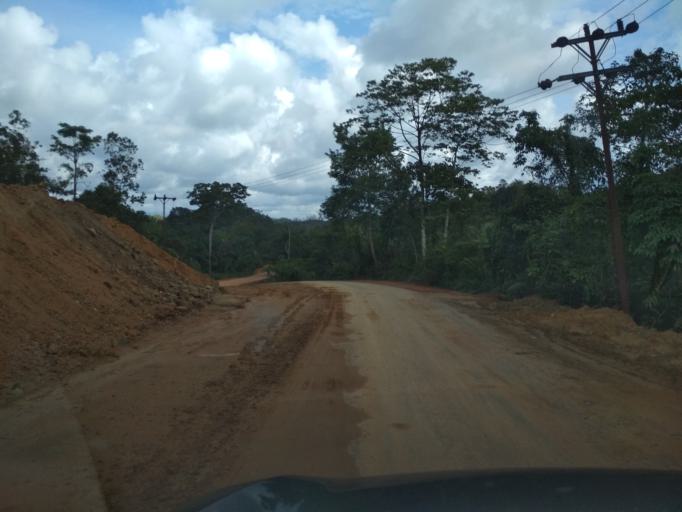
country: ID
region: West Kalimantan
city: Tayan
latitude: 0.5369
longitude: 110.0890
